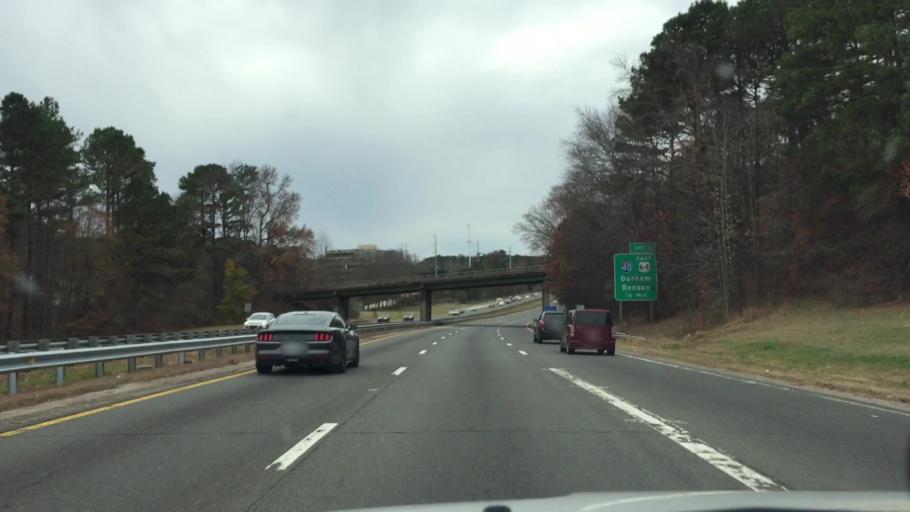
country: US
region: North Carolina
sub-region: Wake County
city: West Raleigh
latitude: 35.7713
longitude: -78.7217
